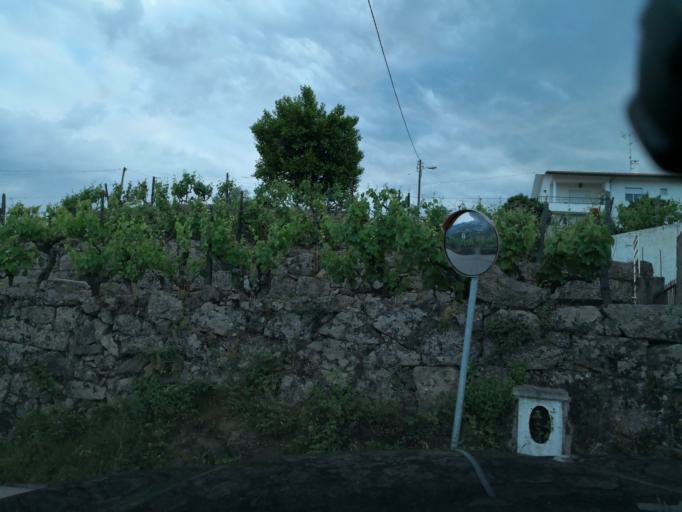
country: PT
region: Vila Real
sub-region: Vila Real
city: Vila Real
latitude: 41.3094
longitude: -7.7805
